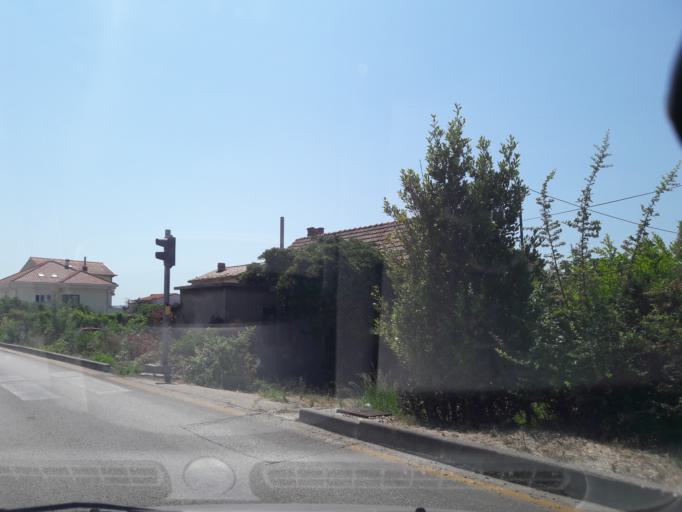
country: HR
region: Splitsko-Dalmatinska
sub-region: Grad Split
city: Split
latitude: 43.5484
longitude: 16.3998
